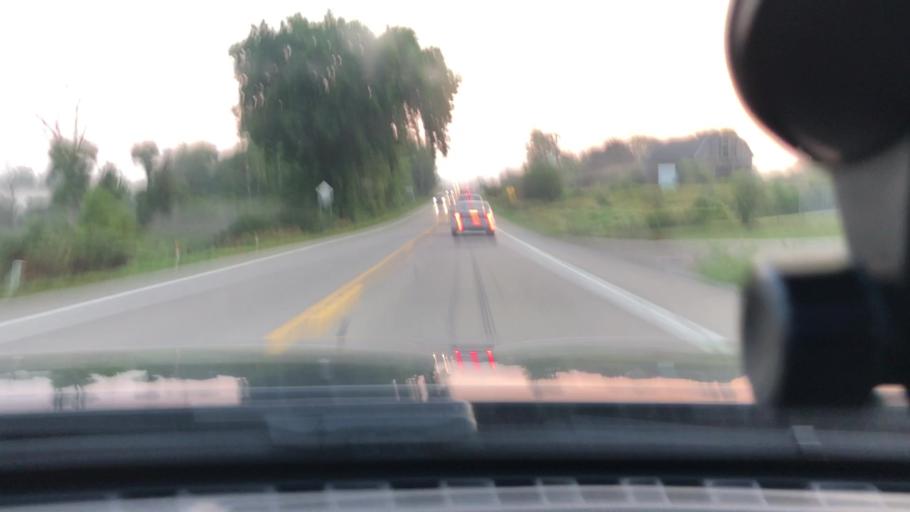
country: US
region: Michigan
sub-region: Washtenaw County
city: Chelsea
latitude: 42.2891
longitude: -84.0301
